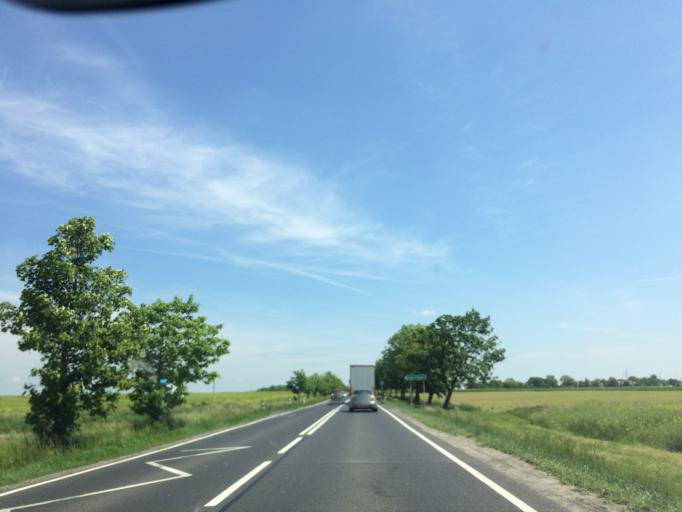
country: PL
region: Lower Silesian Voivodeship
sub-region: Powiat wroclawski
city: Gniechowice
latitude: 51.0068
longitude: 16.8598
